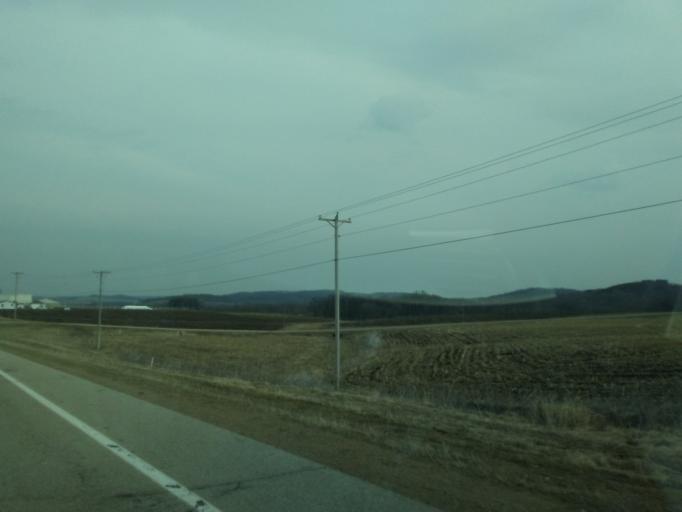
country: US
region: Wisconsin
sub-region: Columbia County
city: Lodi
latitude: 43.2636
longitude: -89.5211
